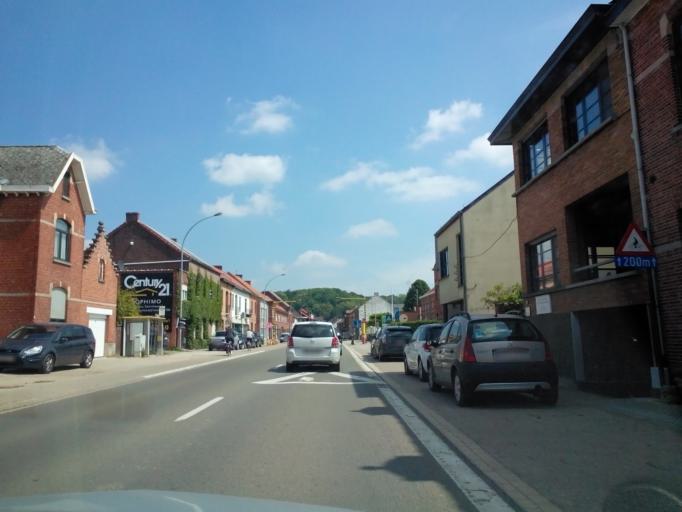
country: BE
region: Flanders
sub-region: Provincie Vlaams-Brabant
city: Holsbeek
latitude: 50.9473
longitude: 4.7514
